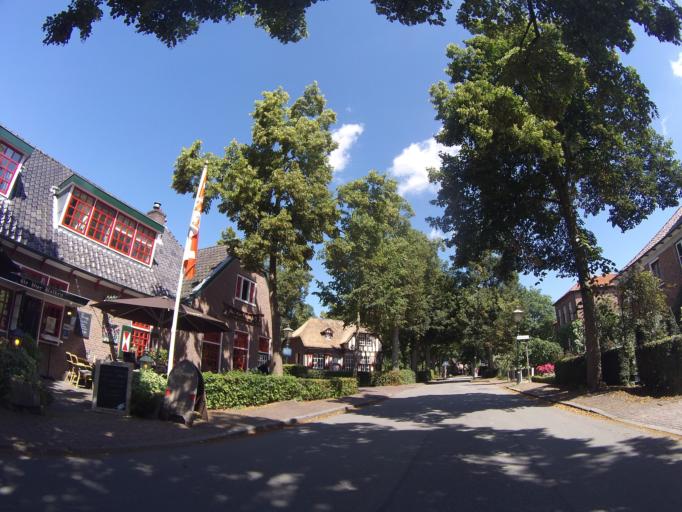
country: NL
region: Utrecht
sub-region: Stichtse Vecht
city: Spechtenkamp
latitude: 52.1199
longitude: 4.9978
